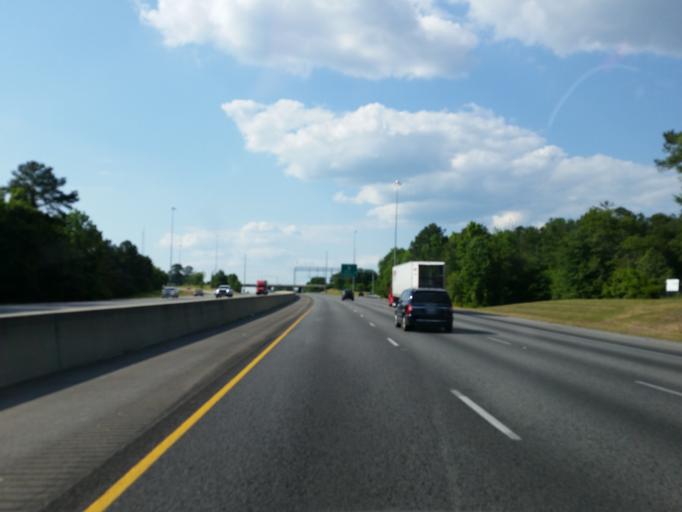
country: US
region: Georgia
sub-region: Bibb County
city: West Point
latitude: 32.8284
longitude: -83.7316
